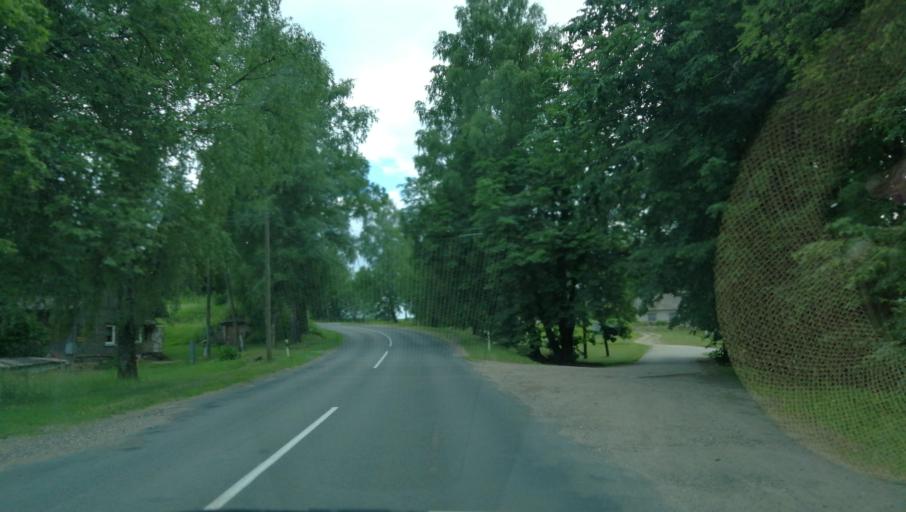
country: LV
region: Rujienas
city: Rujiena
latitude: 57.8850
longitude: 25.3531
